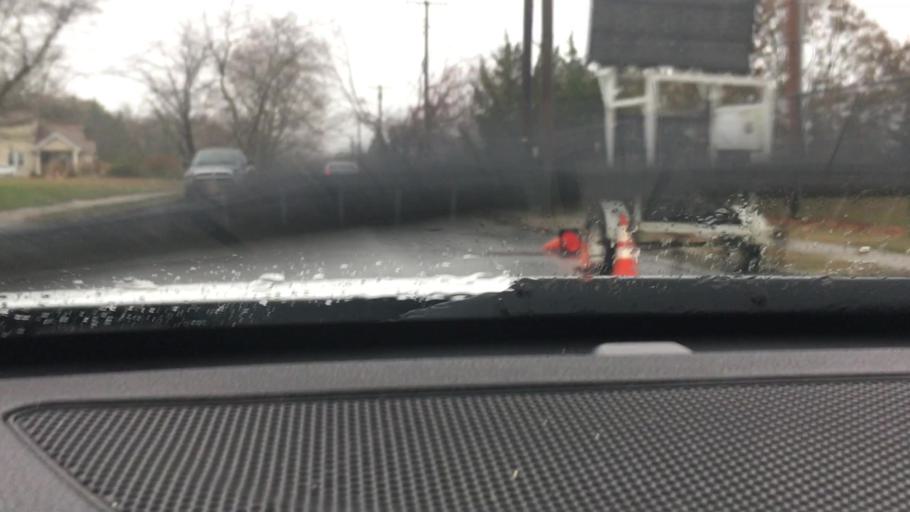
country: US
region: New Jersey
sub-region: Atlantic County
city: Pleasantville
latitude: 39.4025
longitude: -74.5286
